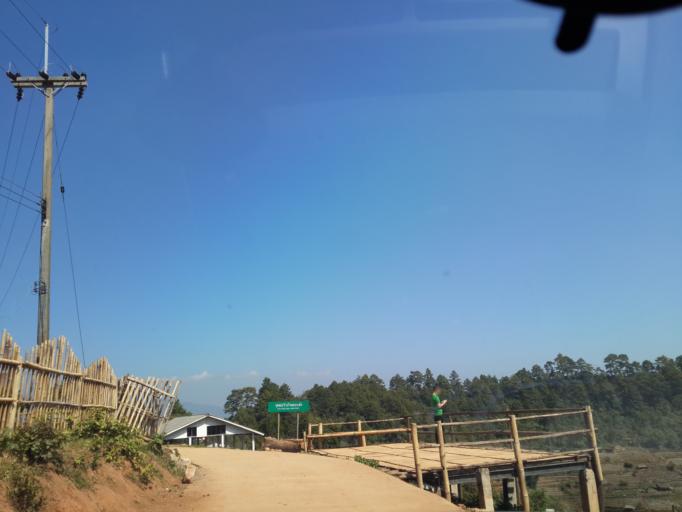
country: TH
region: Chiang Mai
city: Fang
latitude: 19.9268
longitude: 99.0526
